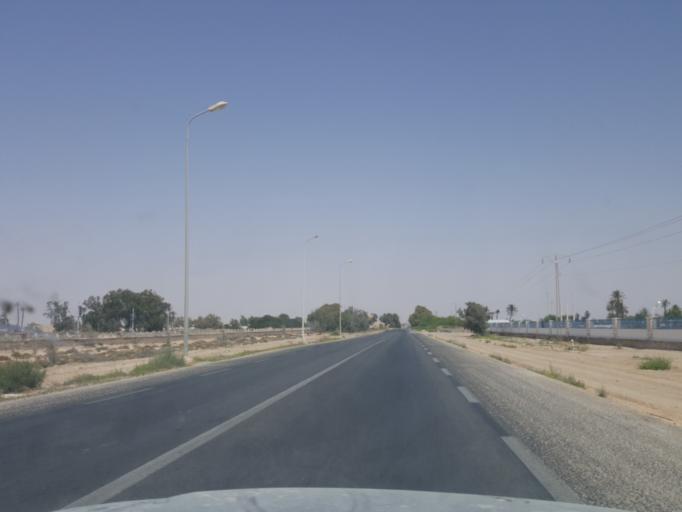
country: TN
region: Qabis
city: Gabes
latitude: 33.9816
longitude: 10.0060
